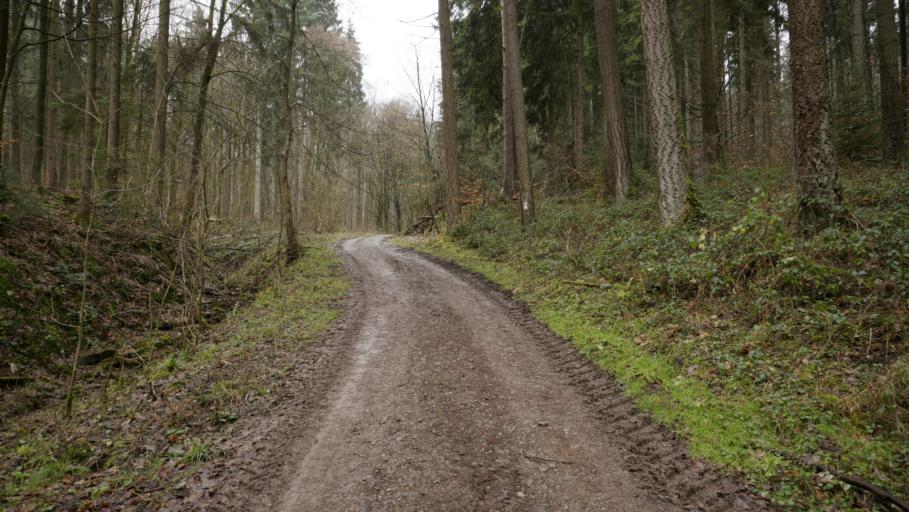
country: DE
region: Baden-Wuerttemberg
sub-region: Karlsruhe Region
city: Zwingenberg
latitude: 49.4029
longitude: 9.0359
